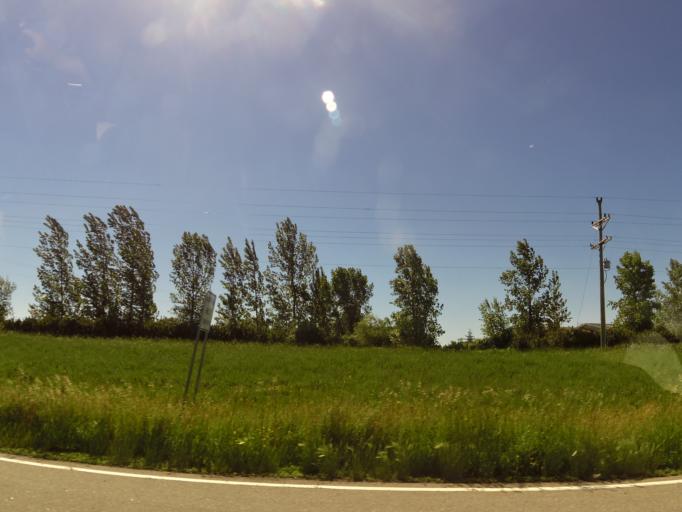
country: US
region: Minnesota
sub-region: Polk County
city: Crookston
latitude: 47.7582
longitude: -96.5475
